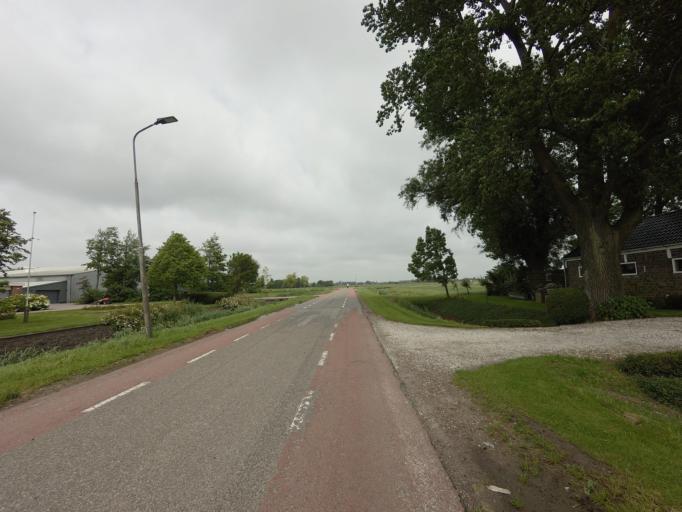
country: NL
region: North Holland
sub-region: Gemeente Schagen
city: Schagen
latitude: 52.7687
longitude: 4.7846
